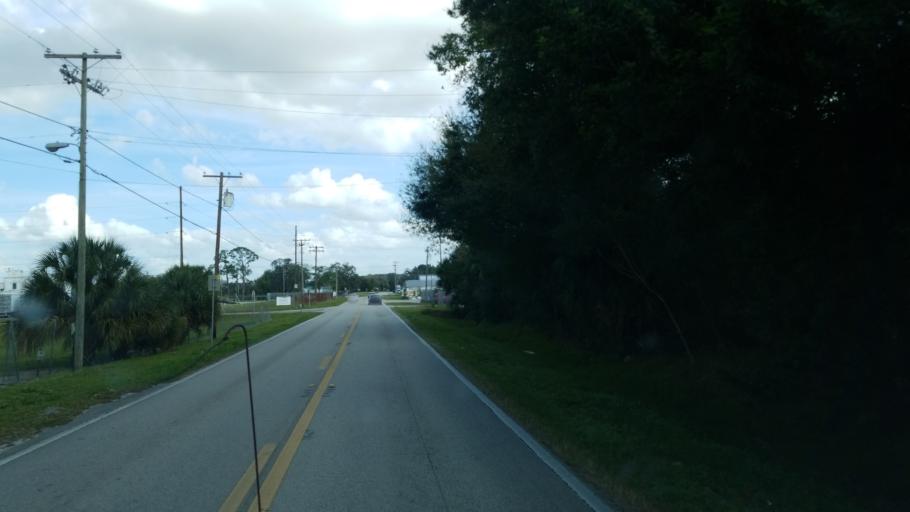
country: US
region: Florida
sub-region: Polk County
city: Dundee
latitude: 27.9790
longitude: -81.6173
